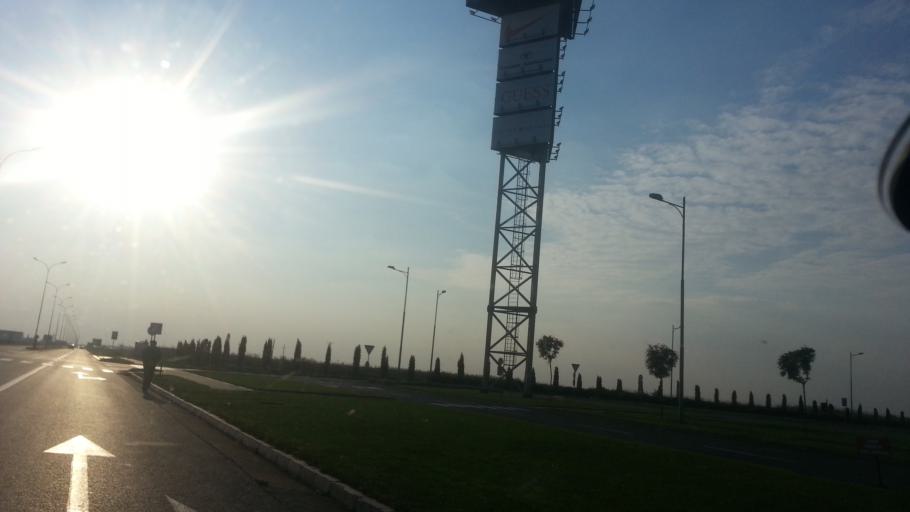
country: RS
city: Novi Karlovci
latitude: 45.0674
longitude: 20.1367
